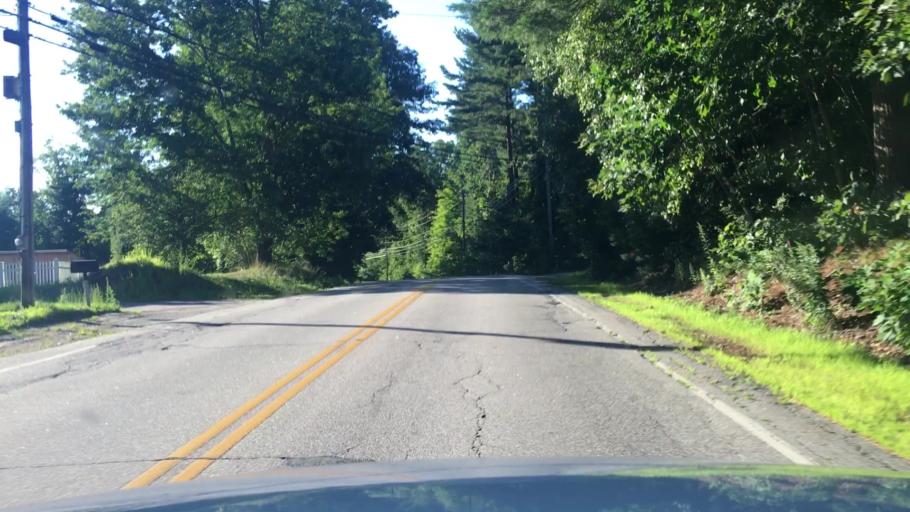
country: US
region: New Hampshire
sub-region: Rockingham County
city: Sandown
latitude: 42.9196
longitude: -71.1695
